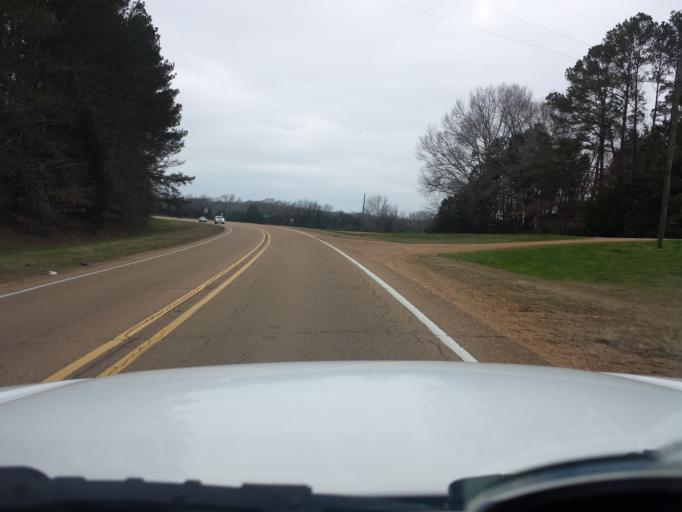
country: US
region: Mississippi
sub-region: Madison County
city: Canton
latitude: 32.7340
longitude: -90.1045
